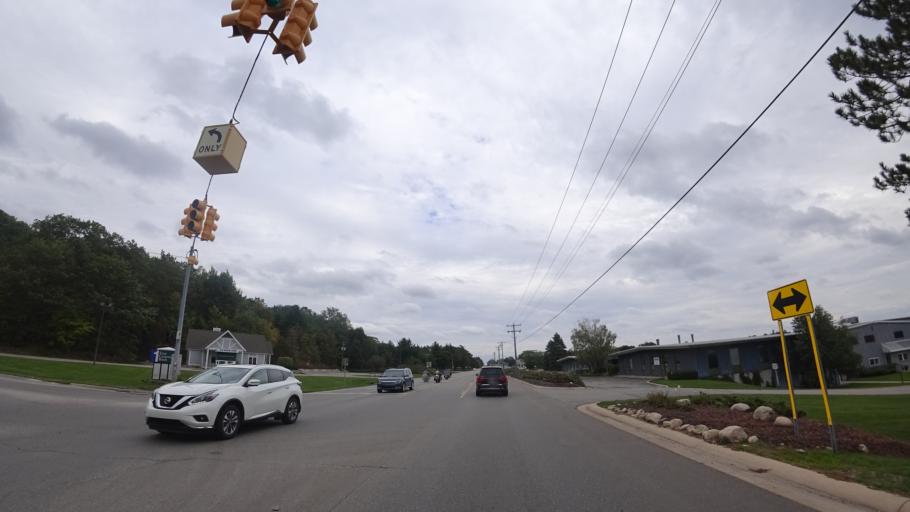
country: US
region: Michigan
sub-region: Emmet County
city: Petoskey
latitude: 45.4278
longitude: -84.9127
